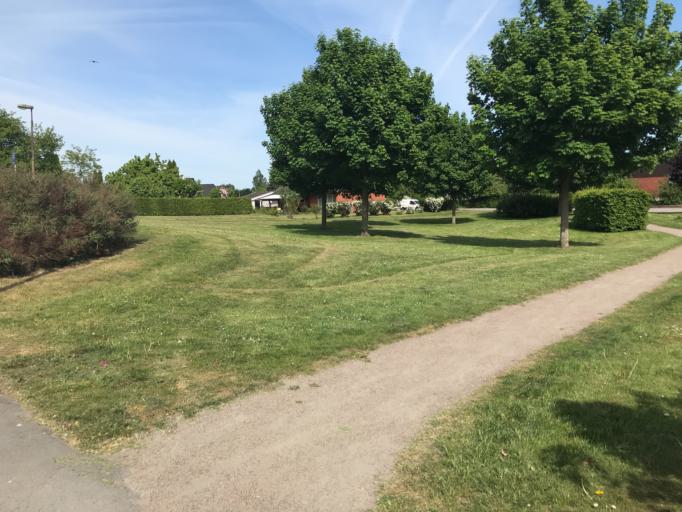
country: SE
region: Skane
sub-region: Malmo
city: Oxie
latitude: 55.5494
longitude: 13.0990
